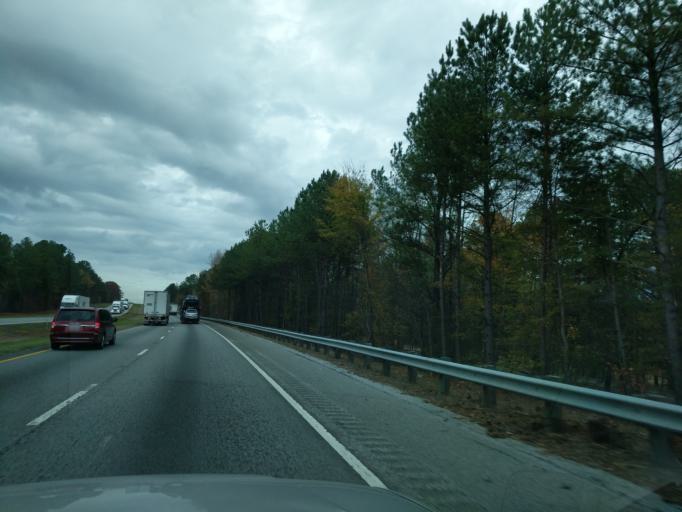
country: US
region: South Carolina
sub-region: Spartanburg County
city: Woodruff
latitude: 34.7142
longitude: -81.9432
